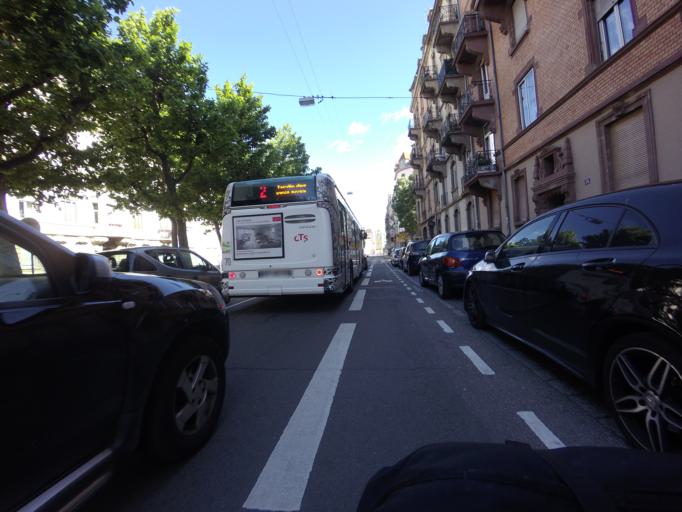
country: FR
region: Alsace
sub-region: Departement du Bas-Rhin
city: Strasbourg
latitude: 48.5780
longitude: 7.7314
